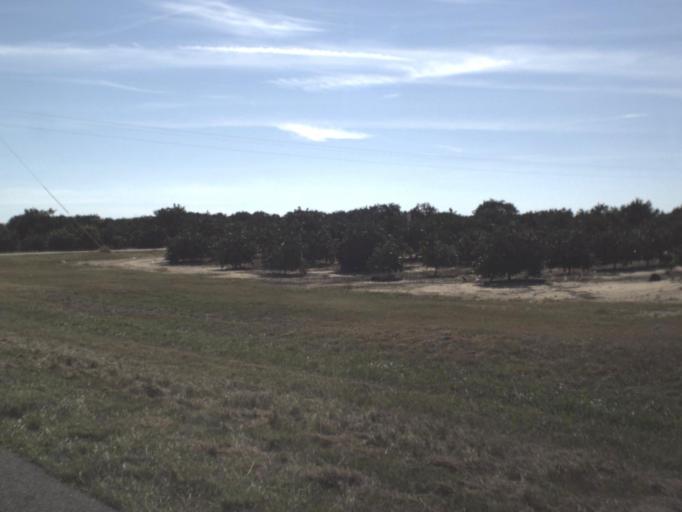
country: US
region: Florida
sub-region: Highlands County
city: Placid Lakes
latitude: 27.1540
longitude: -81.3289
